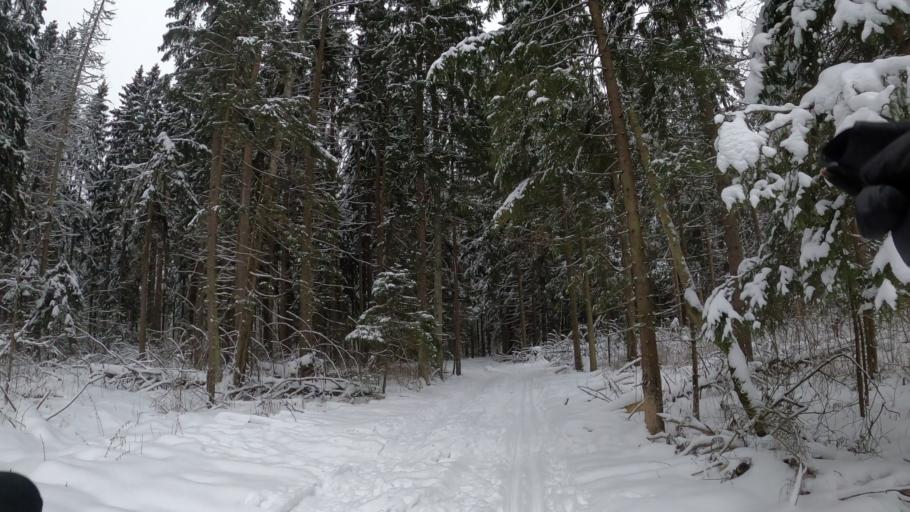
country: RU
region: Moskovskaya
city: Firsanovka
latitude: 55.9611
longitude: 37.2257
